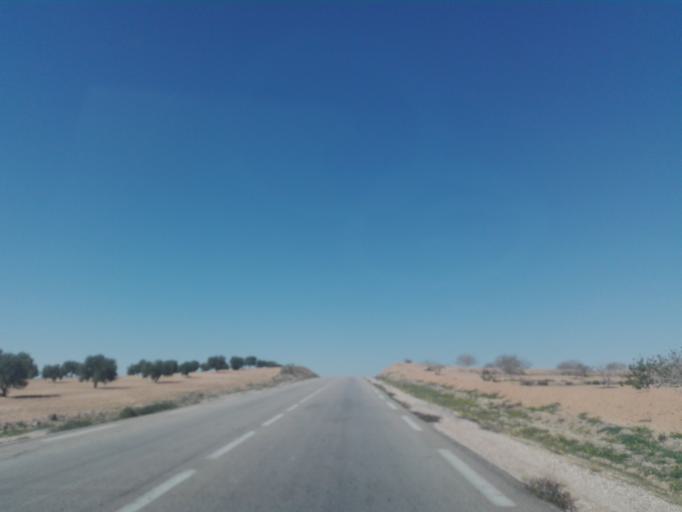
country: TN
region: Safaqis
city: Bi'r `Ali Bin Khalifah
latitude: 34.7578
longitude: 10.2809
